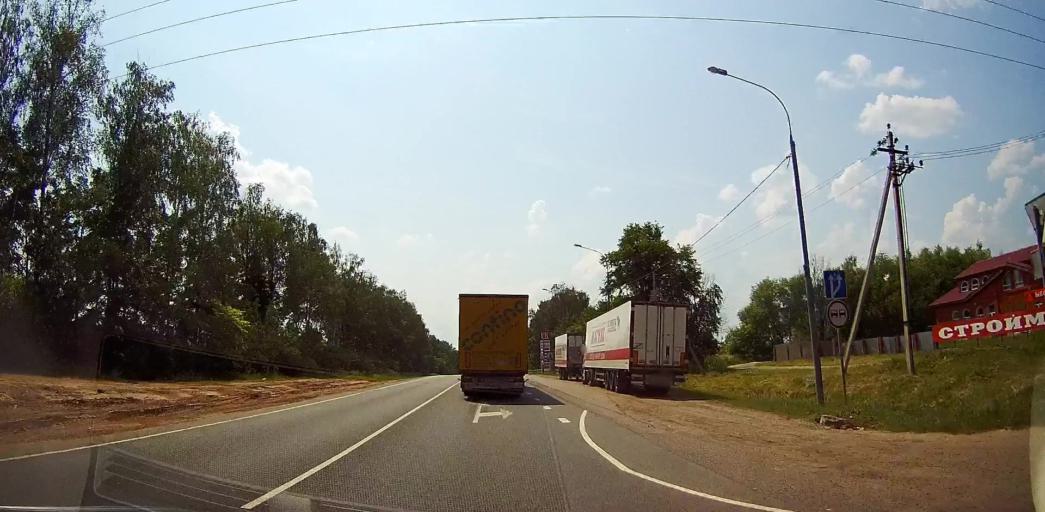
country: RU
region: Moskovskaya
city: Meshcherino
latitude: 55.2008
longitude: 38.3738
